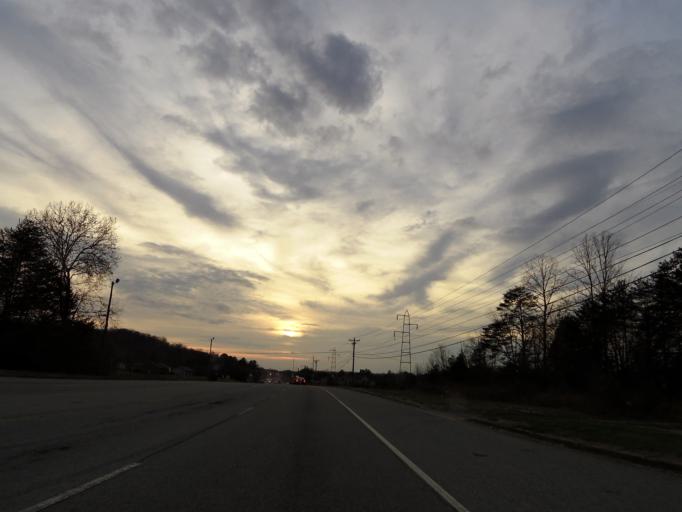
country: US
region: Tennessee
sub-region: Monroe County
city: Vonore
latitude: 35.5810
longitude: -84.2658
